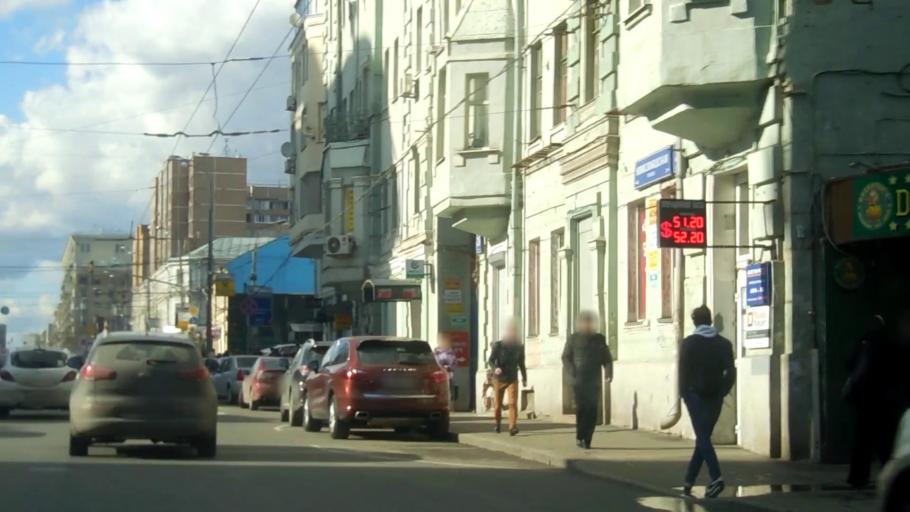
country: RU
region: Moscow
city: Mar'ina Roshcha
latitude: 55.7828
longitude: 37.5979
